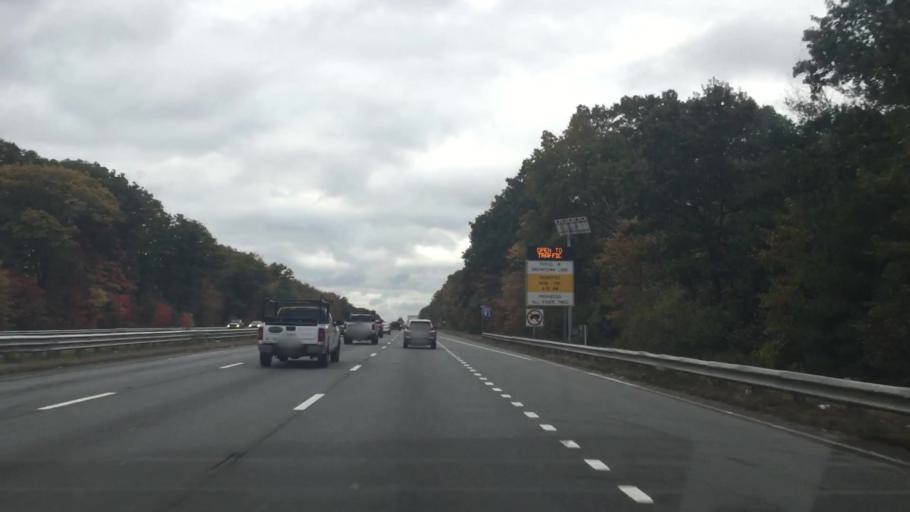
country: US
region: Massachusetts
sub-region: Essex County
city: Methuen
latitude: 42.6897
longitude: -71.2061
